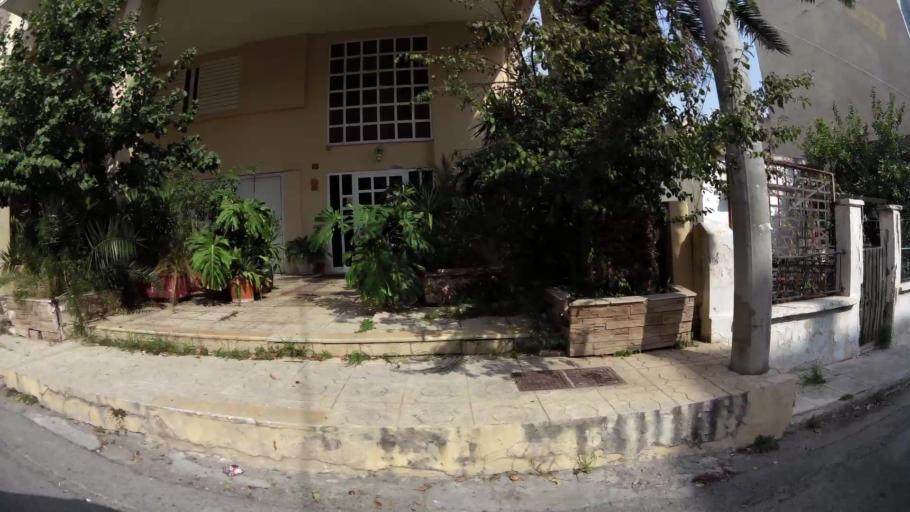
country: GR
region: Attica
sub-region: Nomarchia Athinas
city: Chaidari
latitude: 38.0184
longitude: 23.6710
